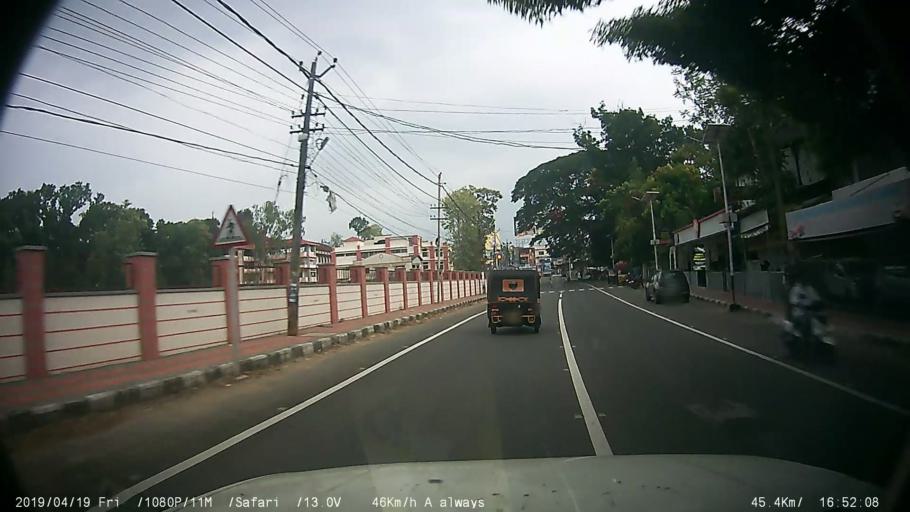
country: IN
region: Kerala
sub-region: Kottayam
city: Changanacheri
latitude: 9.4528
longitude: 76.5369
